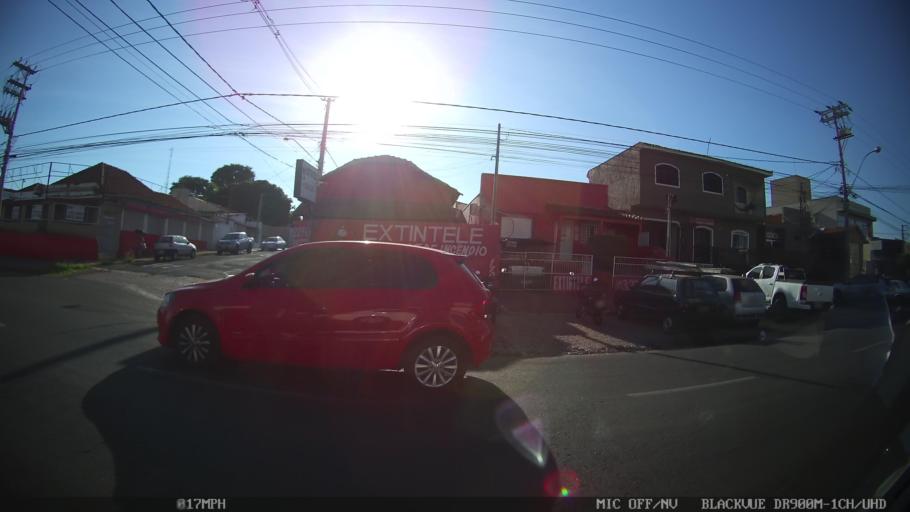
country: BR
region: Sao Paulo
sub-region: Sao Jose Do Rio Preto
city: Sao Jose do Rio Preto
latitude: -20.8105
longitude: -49.3906
